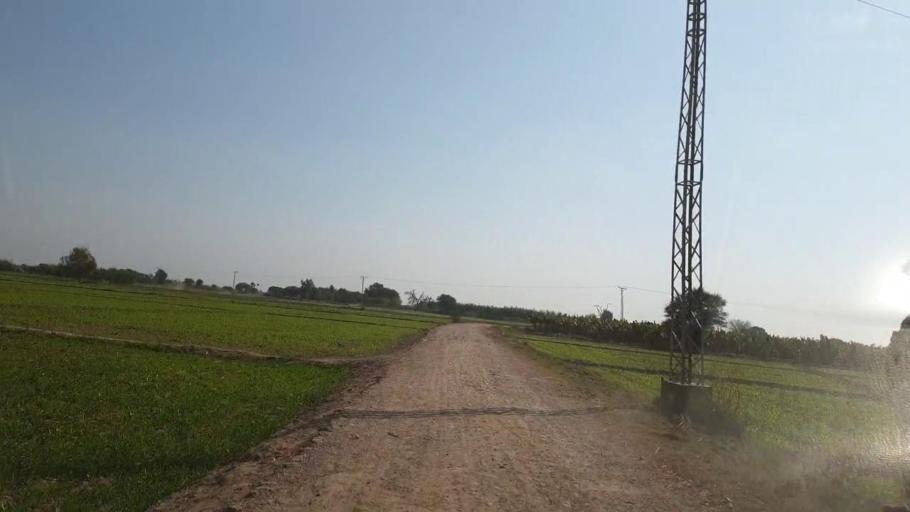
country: PK
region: Sindh
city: Matiari
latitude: 25.5060
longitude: 68.4759
